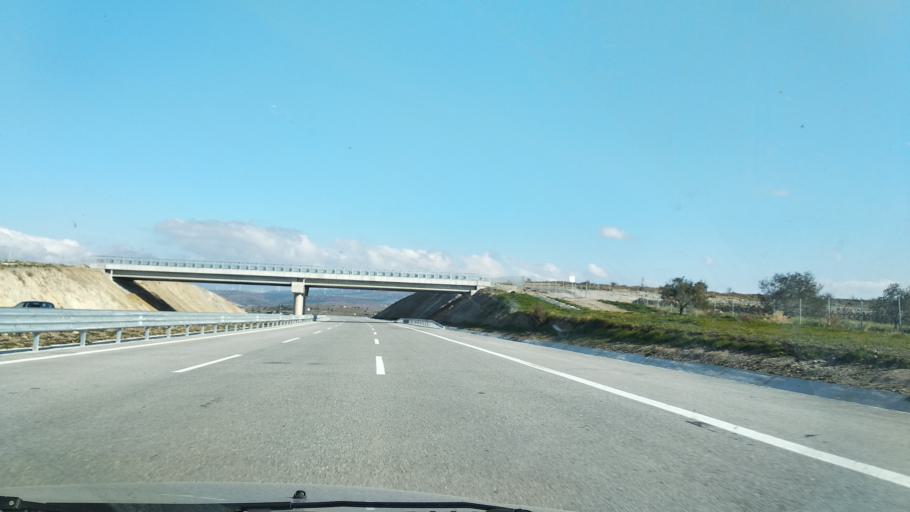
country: TR
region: Izmir
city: Yenisakran
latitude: 38.8595
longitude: 27.0714
